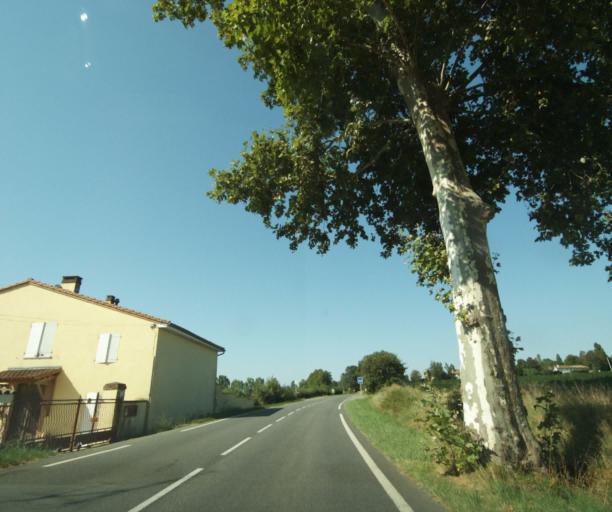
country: FR
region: Midi-Pyrenees
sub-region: Departement de la Haute-Garonne
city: Beaumont-sur-Leze
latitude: 43.3828
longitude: 1.3464
